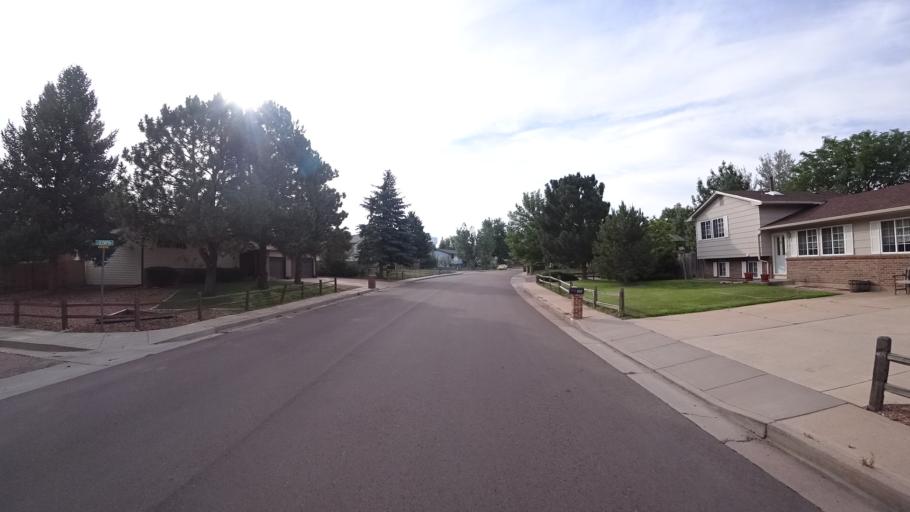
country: US
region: Colorado
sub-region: El Paso County
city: Security-Widefield
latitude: 38.7326
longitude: -104.6944
